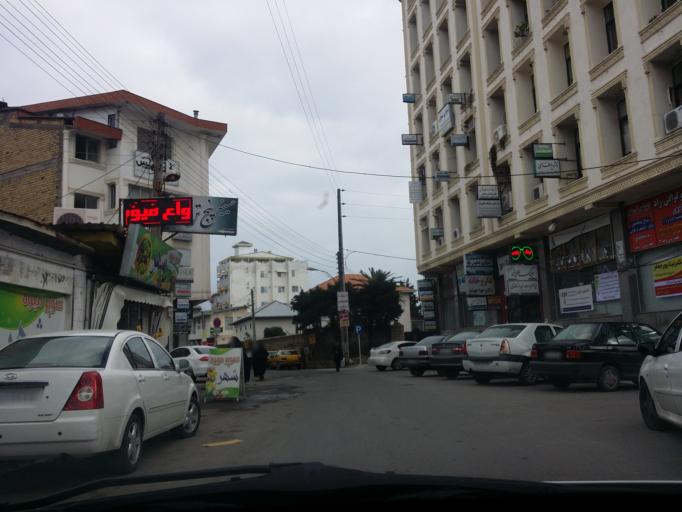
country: IR
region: Mazandaran
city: Chalus
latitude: 36.6571
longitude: 51.4182
